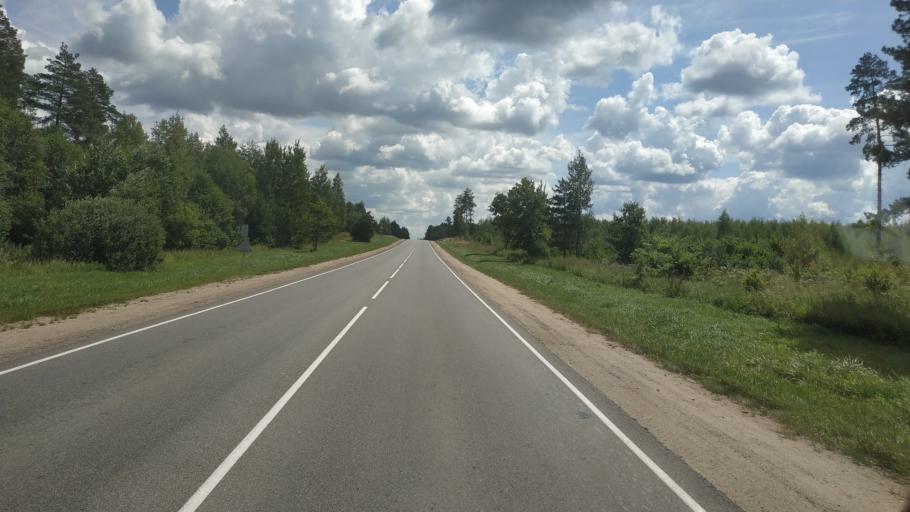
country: BY
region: Mogilev
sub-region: Mahilyowski Rayon
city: Veyno
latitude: 53.8281
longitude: 30.4148
